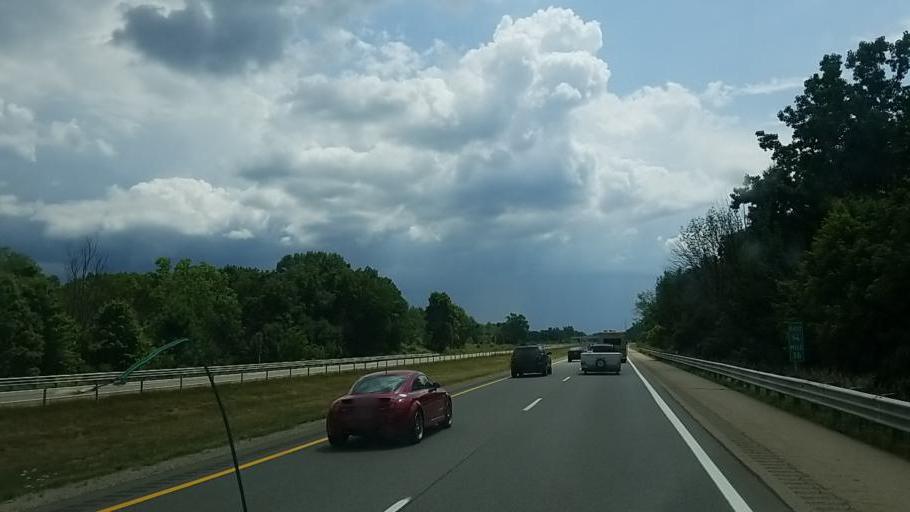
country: US
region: Michigan
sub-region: Kent County
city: East Grand Rapids
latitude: 42.9924
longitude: -85.6053
